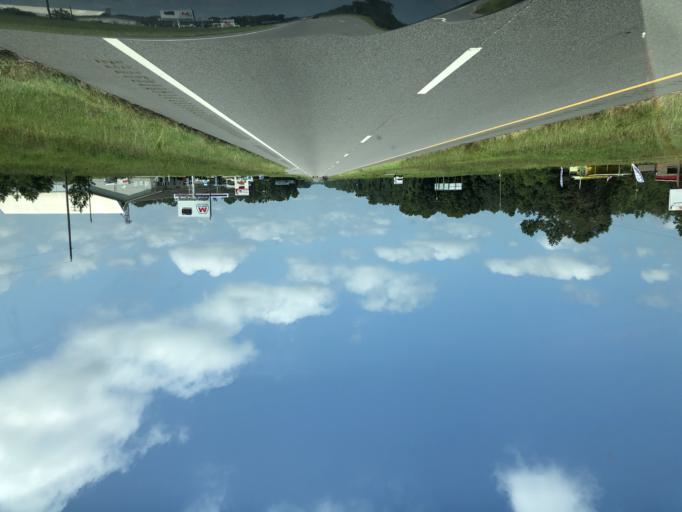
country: US
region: Alabama
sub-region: Houston County
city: Cottonwood
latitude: 31.0186
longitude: -85.4073
